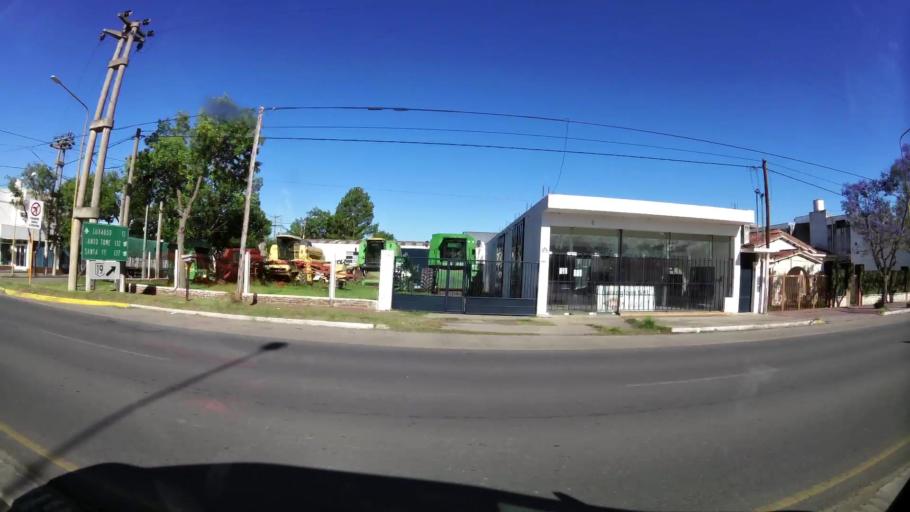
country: AR
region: Cordoba
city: San Francisco
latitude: -31.4170
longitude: -62.0946
